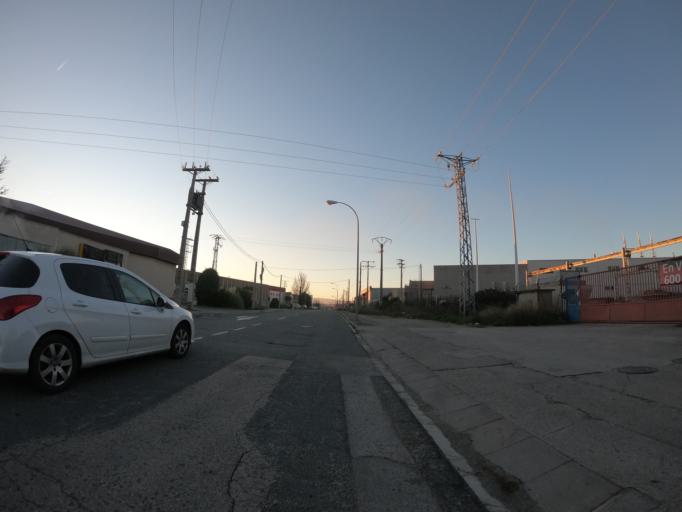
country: ES
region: Basque Country
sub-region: Provincia de Alava
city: Oyon
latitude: 42.4837
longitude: -2.4208
